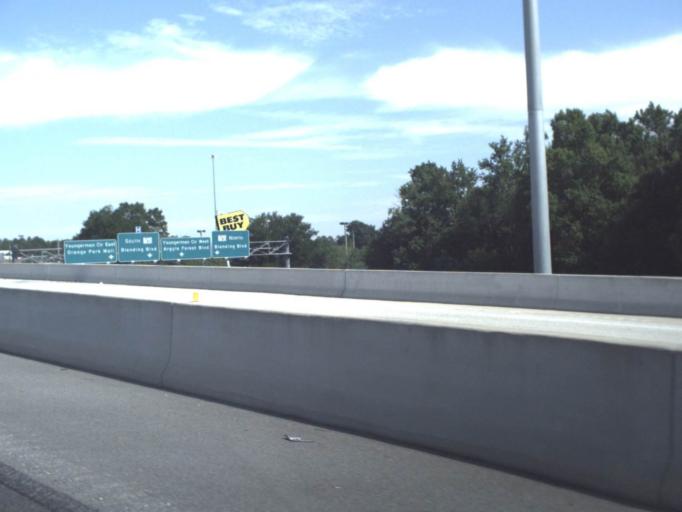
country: US
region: Florida
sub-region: Clay County
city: Bellair-Meadowbrook Terrace
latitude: 30.1960
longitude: -81.7373
